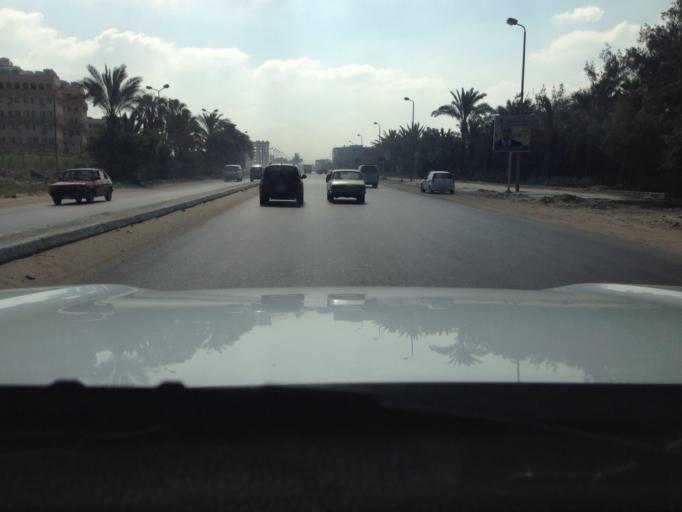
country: EG
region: Alexandria
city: Alexandria
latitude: 31.2039
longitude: 29.9730
